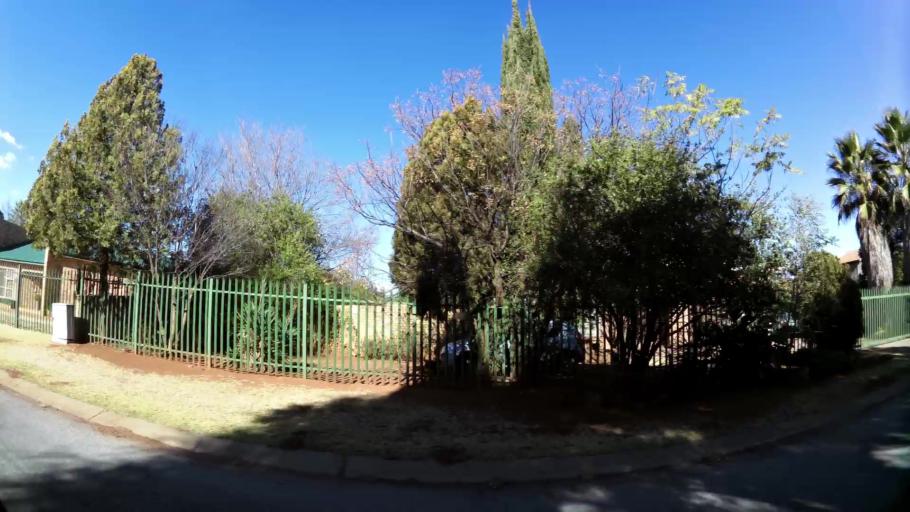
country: ZA
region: Gauteng
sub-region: West Rand District Municipality
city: Carletonville
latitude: -26.3656
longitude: 27.3689
